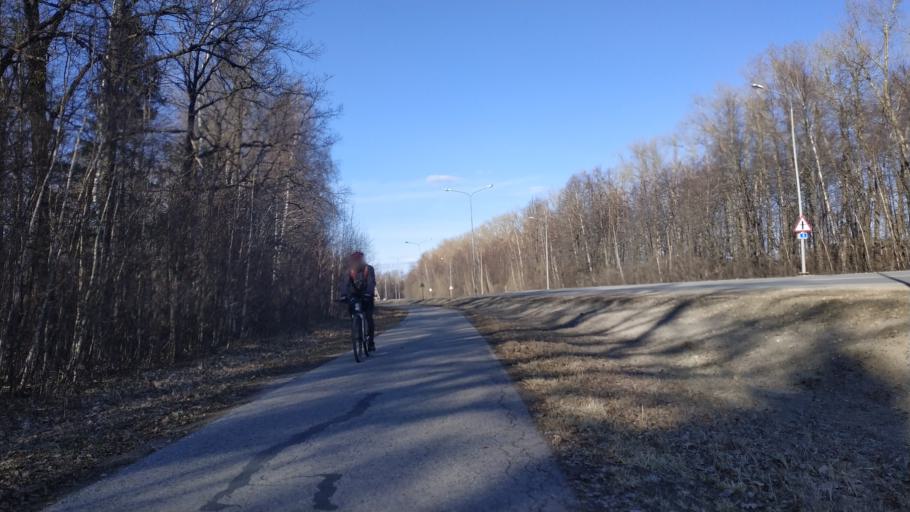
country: RU
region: Chuvashia
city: Ishley
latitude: 56.1284
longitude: 47.0696
